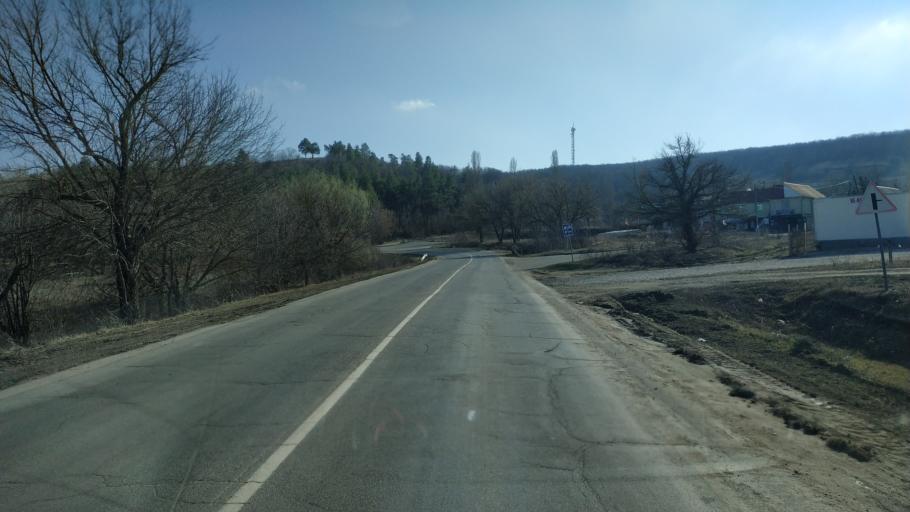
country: MD
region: Hincesti
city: Hincesti
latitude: 46.8332
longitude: 28.5685
